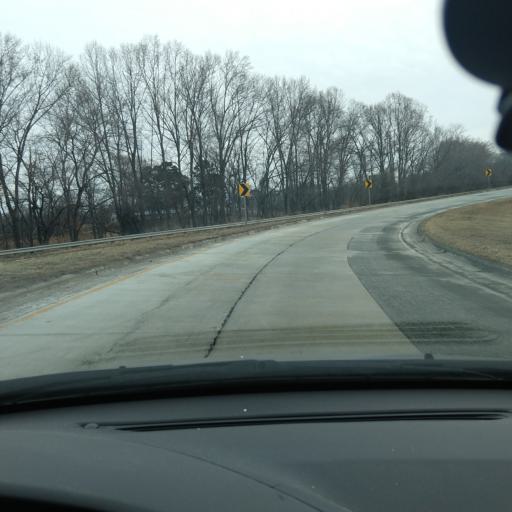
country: US
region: North Carolina
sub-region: Forsyth County
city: Winston-Salem
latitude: 36.0640
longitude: -80.2325
